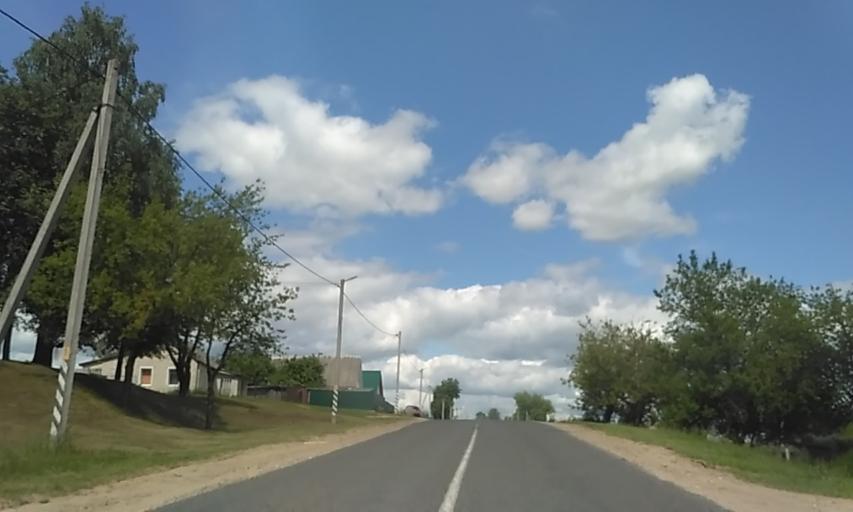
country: BY
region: Minsk
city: Krupki
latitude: 54.3461
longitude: 29.1507
